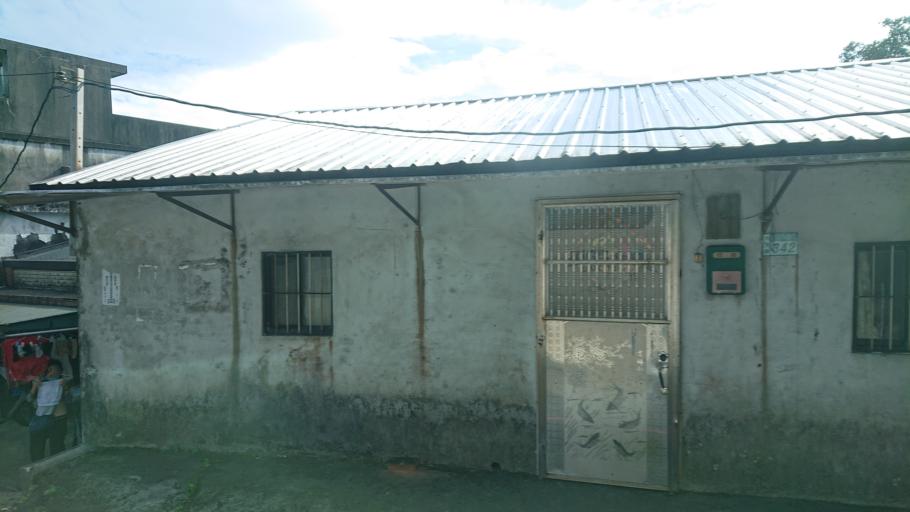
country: TW
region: Taiwan
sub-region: Keelung
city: Keelung
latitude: 25.1101
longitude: 121.8499
